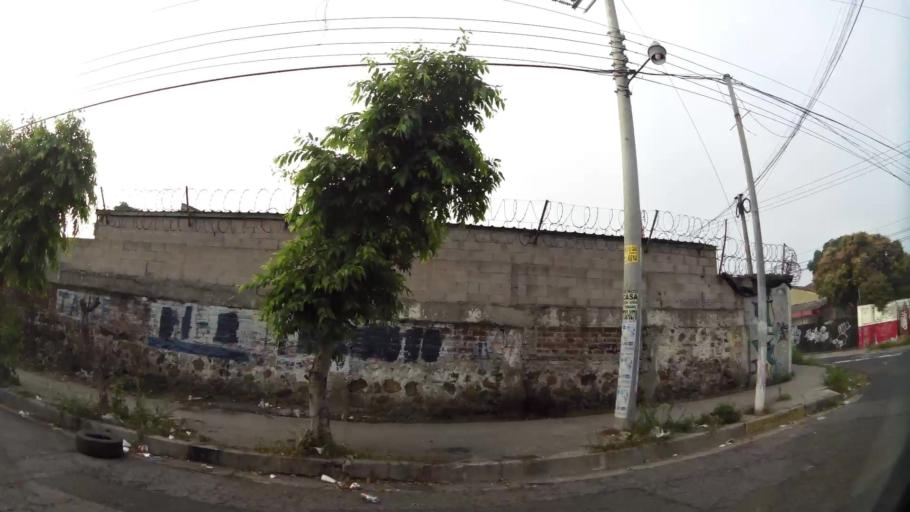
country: SV
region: San Salvador
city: San Salvador
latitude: 13.7061
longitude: -89.1891
